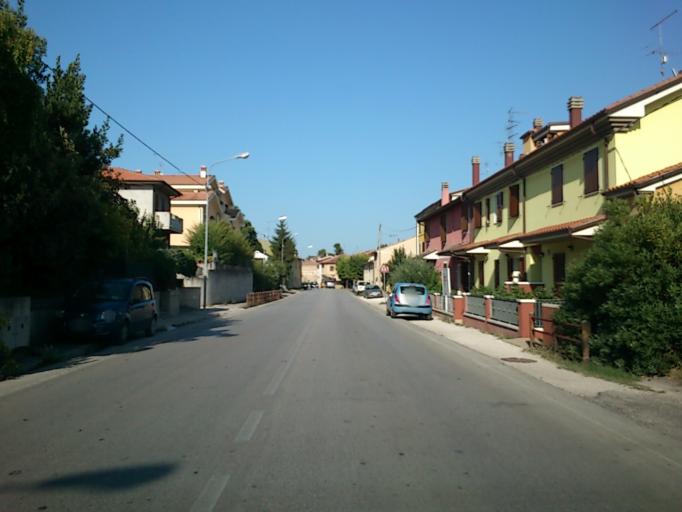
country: IT
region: The Marches
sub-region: Provincia di Pesaro e Urbino
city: Cuccurano
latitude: 43.8004
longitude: 12.9692
